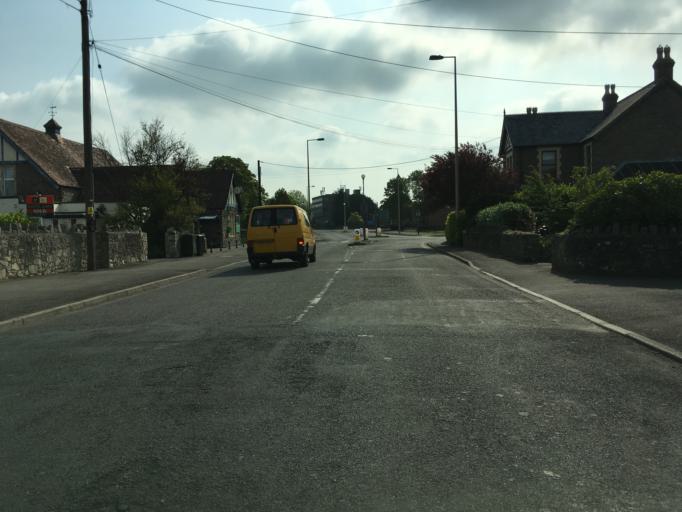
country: GB
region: England
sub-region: North Somerset
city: Nailsea
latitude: 51.4336
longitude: -2.7639
